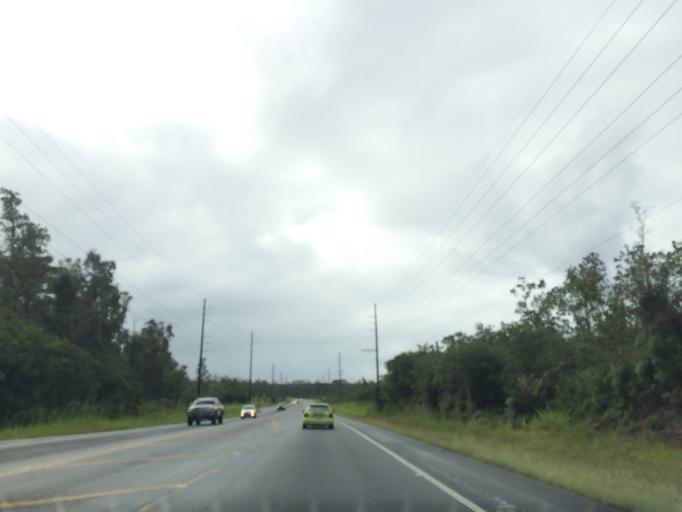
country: US
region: Hawaii
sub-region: Hawaii County
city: Ainaloa
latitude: 19.5320
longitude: -154.9715
